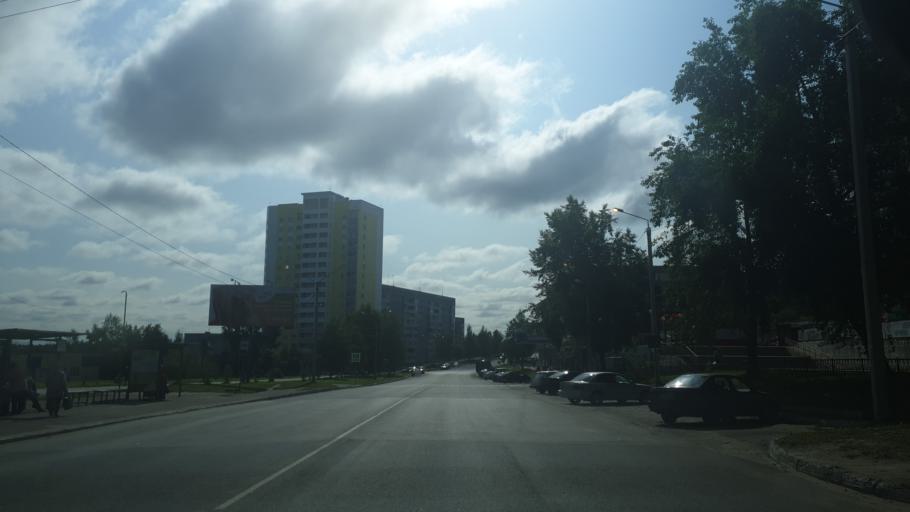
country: RU
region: Komi Republic
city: Ezhva
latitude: 61.7864
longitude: 50.7555
